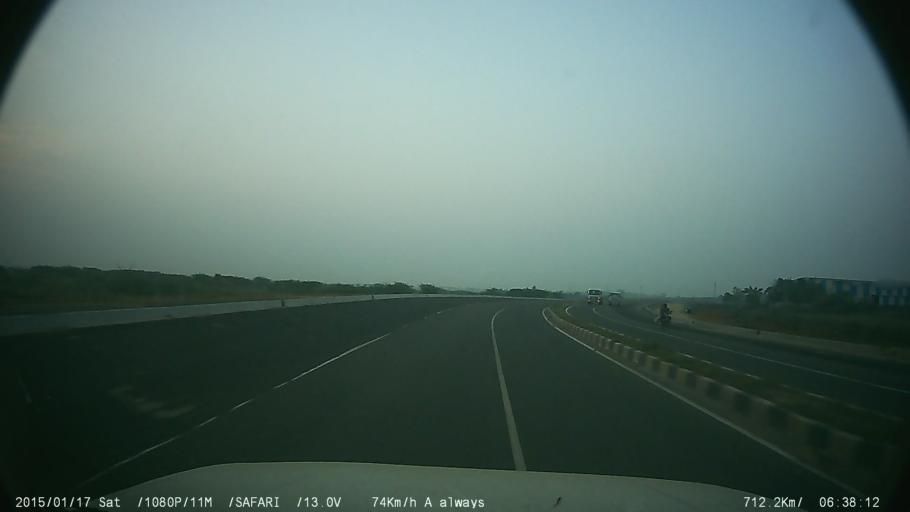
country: IN
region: Tamil Nadu
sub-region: Kancheepuram
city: Sriperumbudur
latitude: 12.9384
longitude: 79.9357
